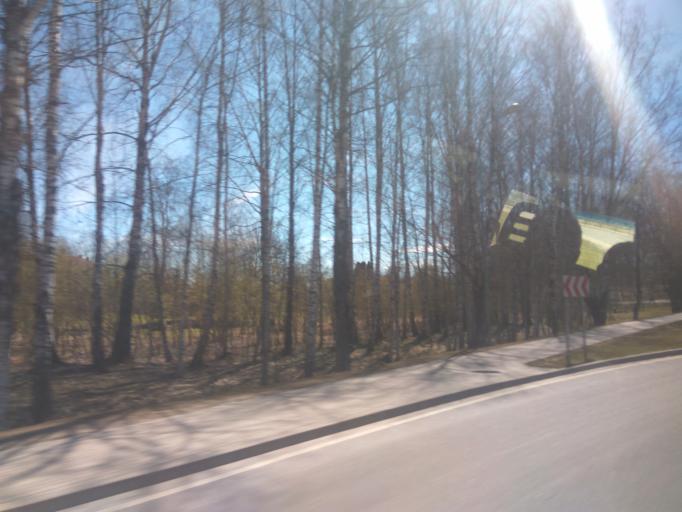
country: LV
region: Aluksnes Rajons
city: Aluksne
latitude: 57.4336
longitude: 27.0390
